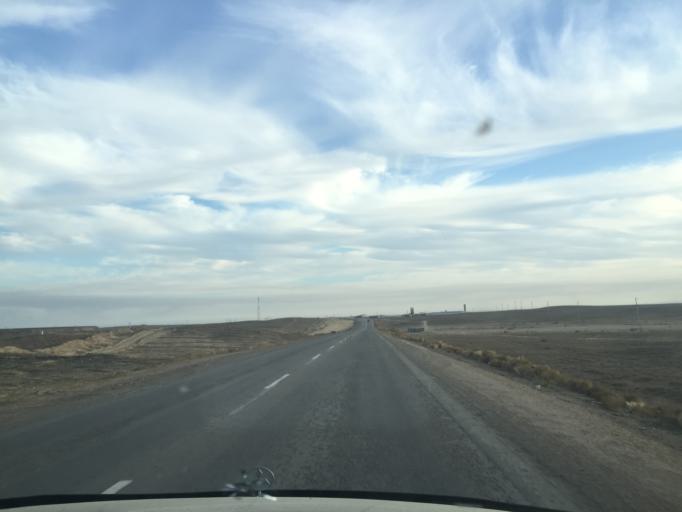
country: KZ
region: Almaty Oblysy
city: Ulken
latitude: 45.1717
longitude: 73.9339
